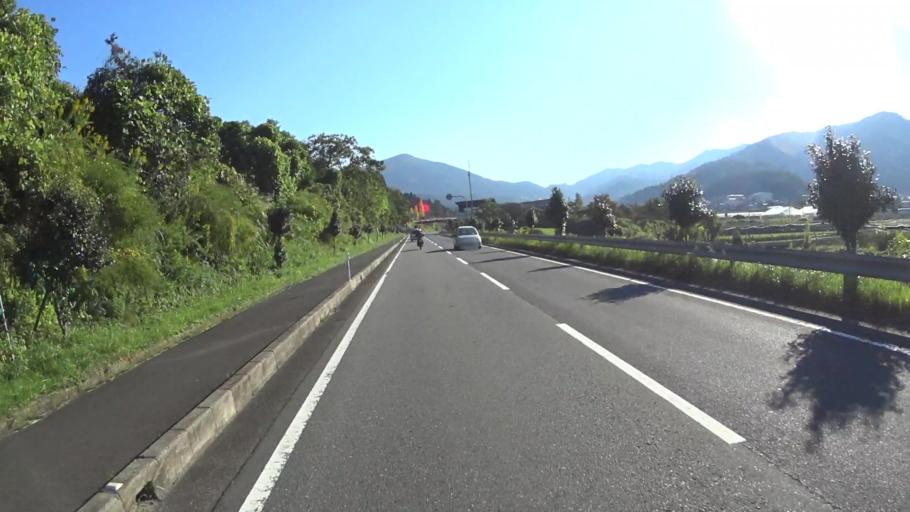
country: JP
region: Kyoto
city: Miyazu
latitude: 35.4844
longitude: 135.0939
